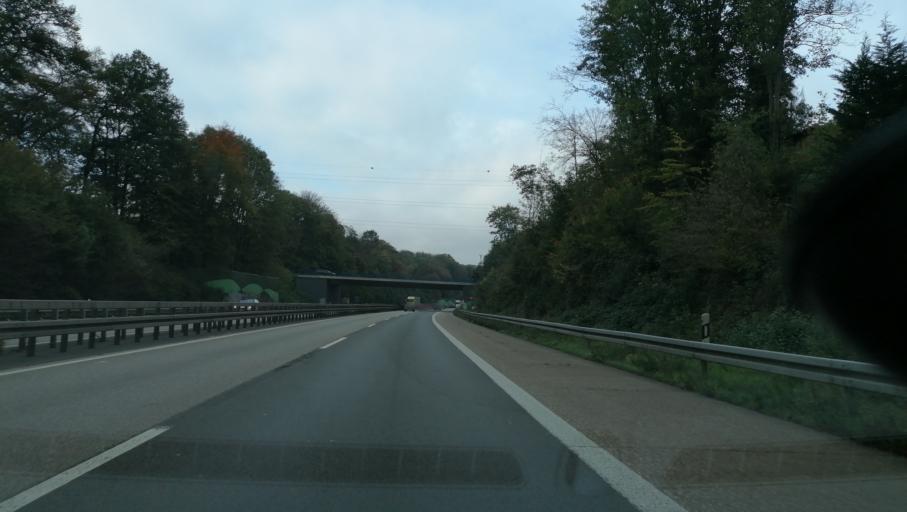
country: DE
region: North Rhine-Westphalia
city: Sprockhovel
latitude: 51.3782
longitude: 7.2638
